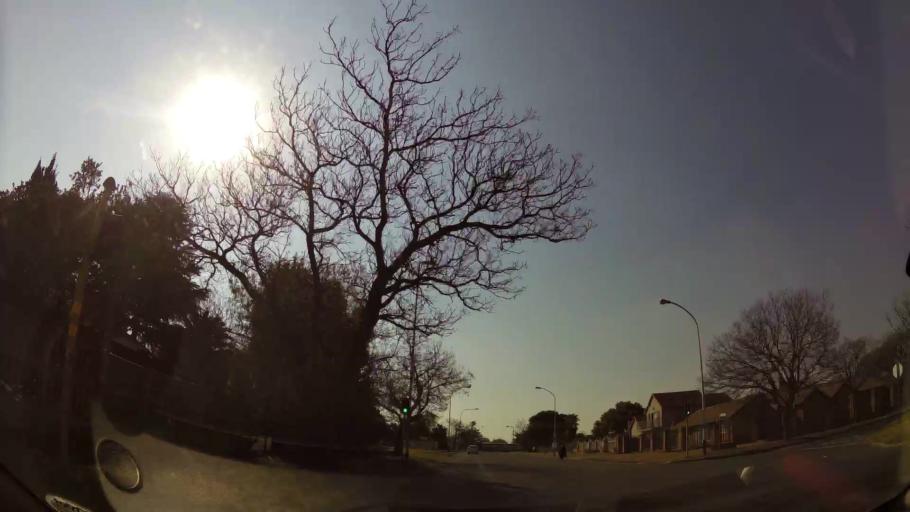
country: ZA
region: Gauteng
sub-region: Ekurhuleni Metropolitan Municipality
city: Boksburg
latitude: -26.1636
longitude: 28.2730
